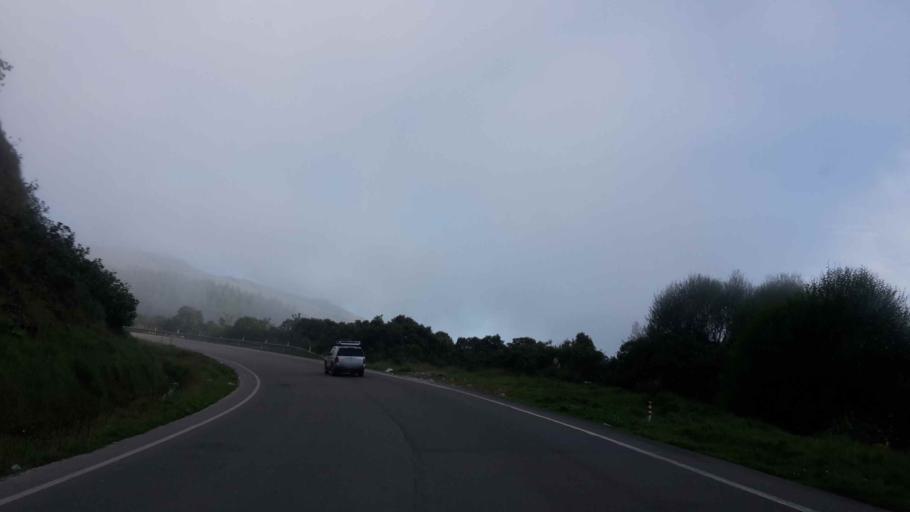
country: BO
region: Cochabamba
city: Colomi
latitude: -17.2204
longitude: -65.8931
